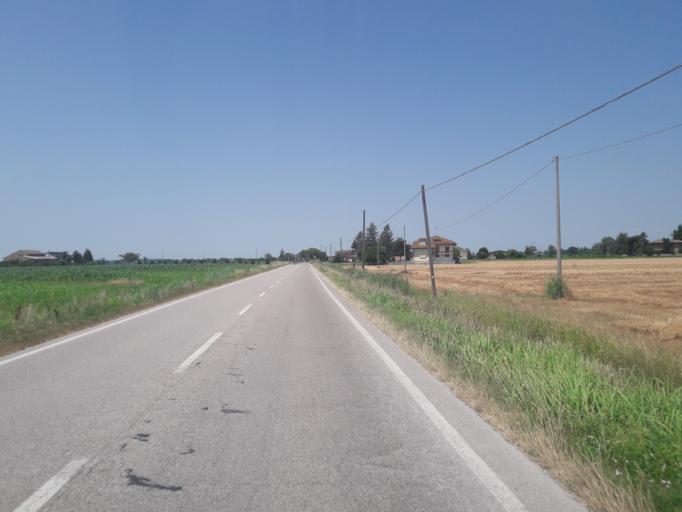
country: IT
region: Veneto
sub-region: Provincia di Rovigo
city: Papozze
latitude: 45.0061
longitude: 12.1512
